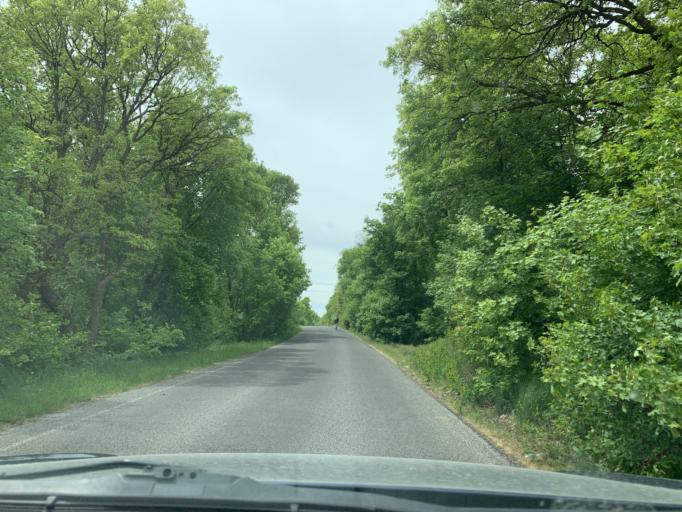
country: US
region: Utah
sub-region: Utah County
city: Mapleton
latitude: 40.1687
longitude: -111.4790
